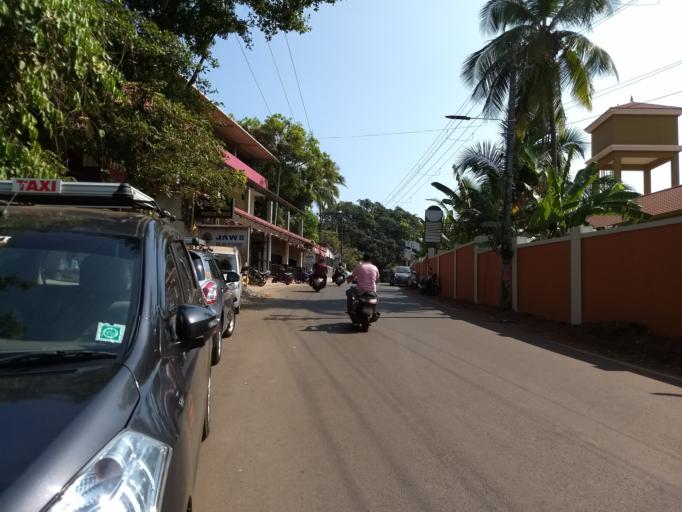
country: IN
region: Goa
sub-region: North Goa
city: Vagator
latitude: 15.5996
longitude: 73.7395
